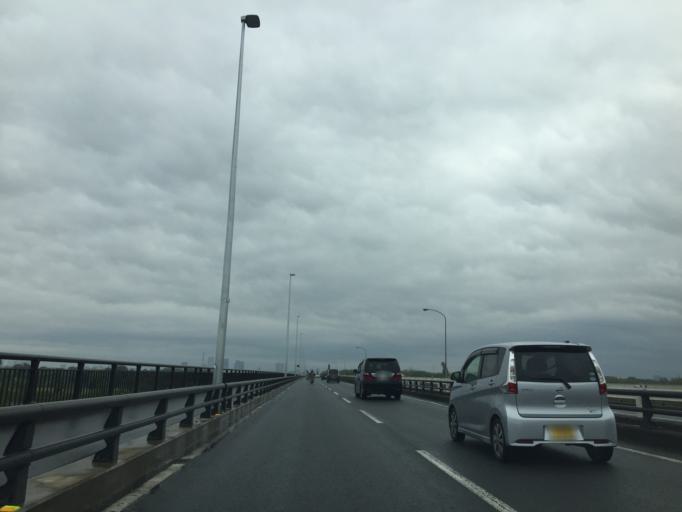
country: JP
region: Saitama
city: Shiki
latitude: 35.8541
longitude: 139.5872
